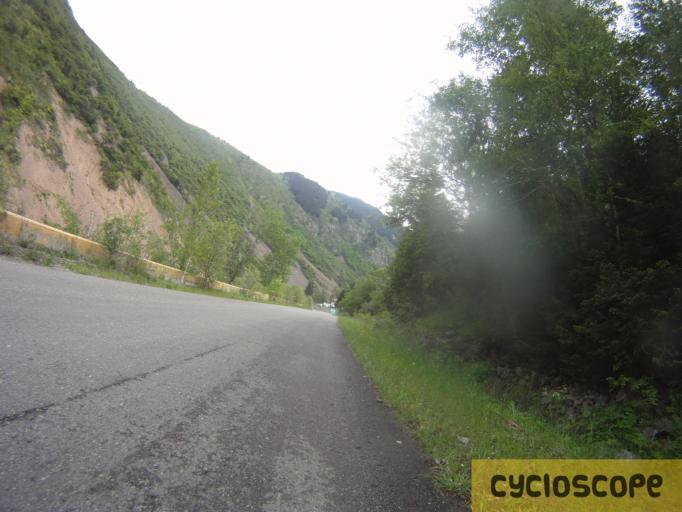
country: KZ
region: Almaty Oblysy
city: Esik
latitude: 43.2719
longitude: 77.5097
